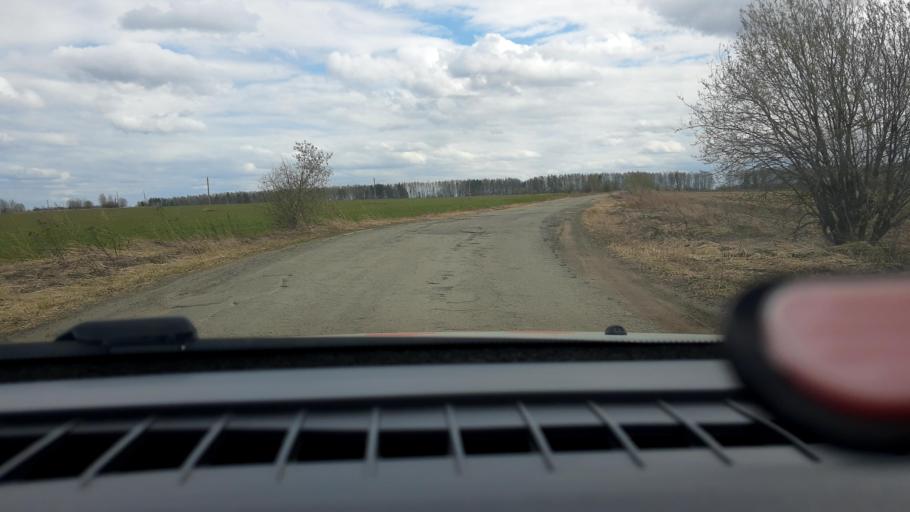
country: RU
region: Nizjnij Novgorod
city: Burevestnik
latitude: 56.1614
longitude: 43.6950
